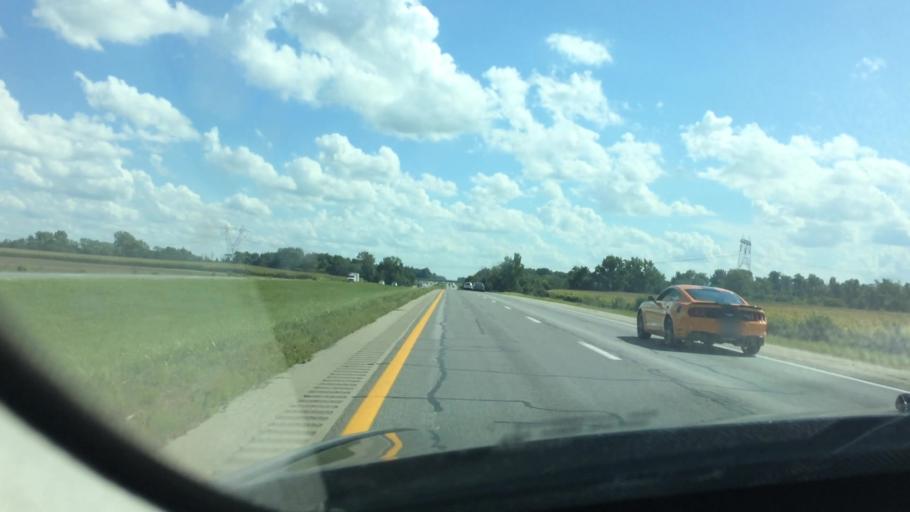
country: US
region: Ohio
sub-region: Auglaize County
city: Wapakoneta
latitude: 40.5343
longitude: -84.1694
